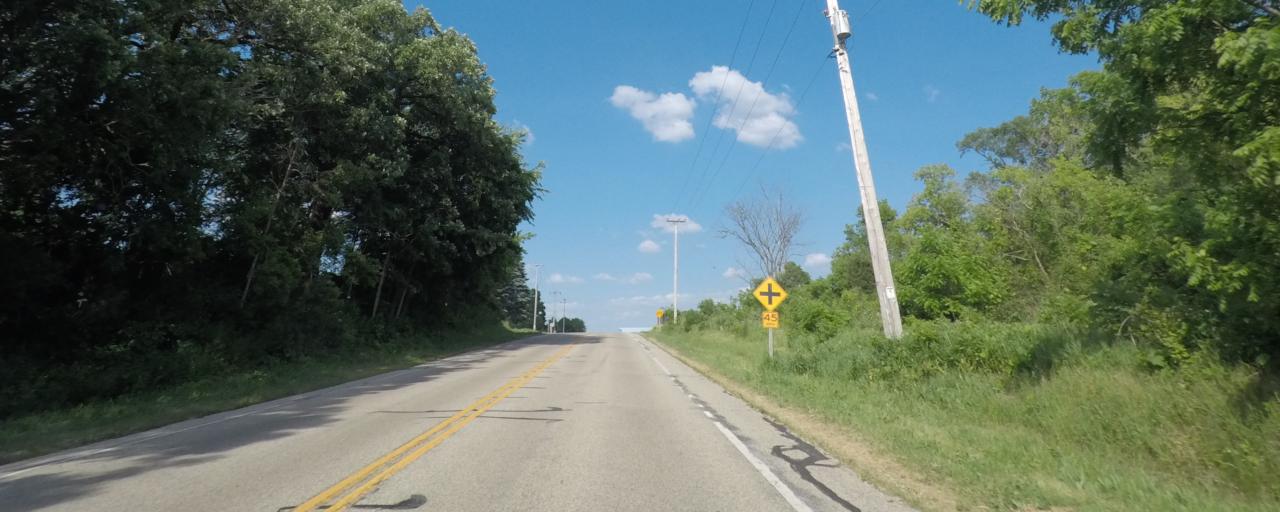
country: US
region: Wisconsin
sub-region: Walworth County
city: Potter Lake
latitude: 42.8143
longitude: -88.3391
